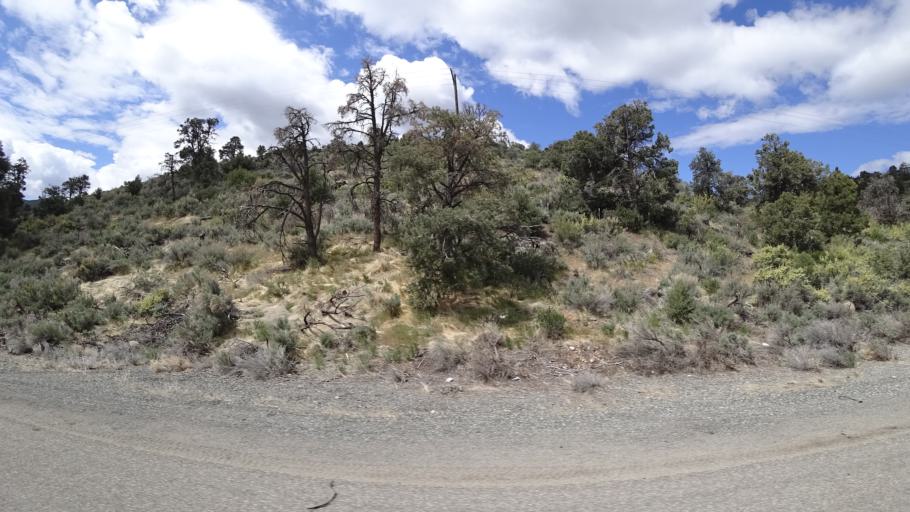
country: US
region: Nevada
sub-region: Douglas County
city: Gardnerville Ranchos
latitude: 38.7596
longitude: -119.5754
